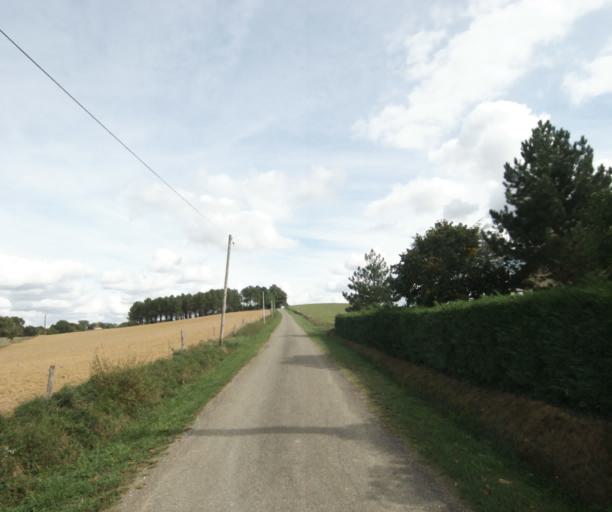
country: FR
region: Midi-Pyrenees
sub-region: Departement du Gers
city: Eauze
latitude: 43.8343
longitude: 0.0854
